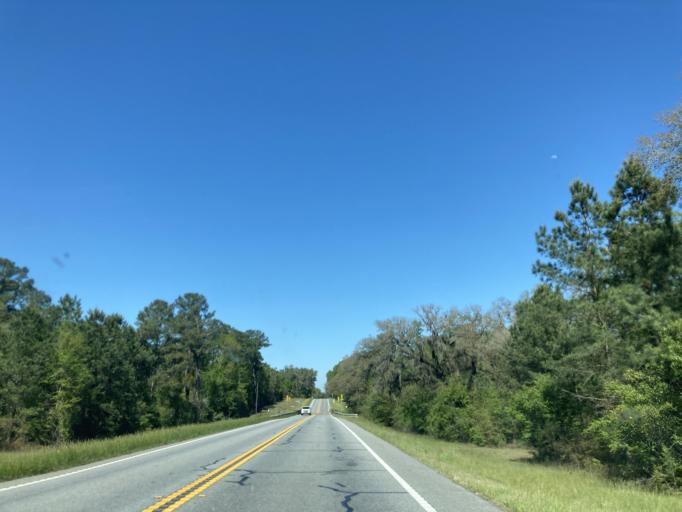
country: US
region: Georgia
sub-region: Baker County
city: Newton
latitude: 31.2031
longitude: -84.4990
